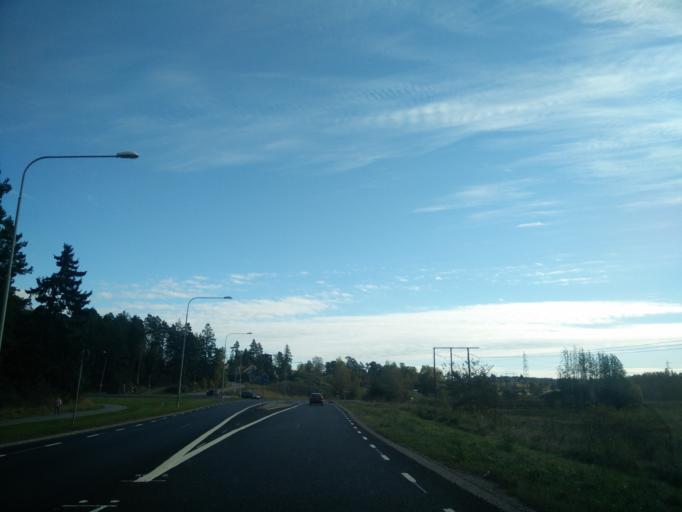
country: SE
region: Stockholm
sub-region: Upplands Vasby Kommun
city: Upplands Vaesby
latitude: 59.5102
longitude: 17.9604
